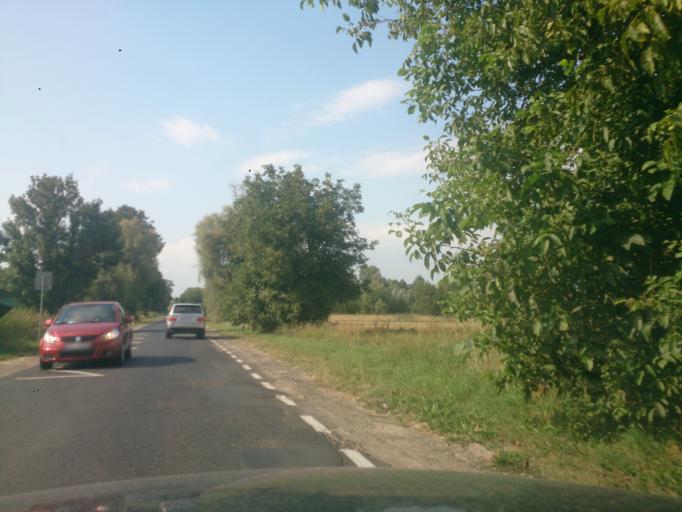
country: PL
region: Swietokrzyskie
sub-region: Powiat sandomierski
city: Klimontow
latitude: 50.6858
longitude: 21.3843
